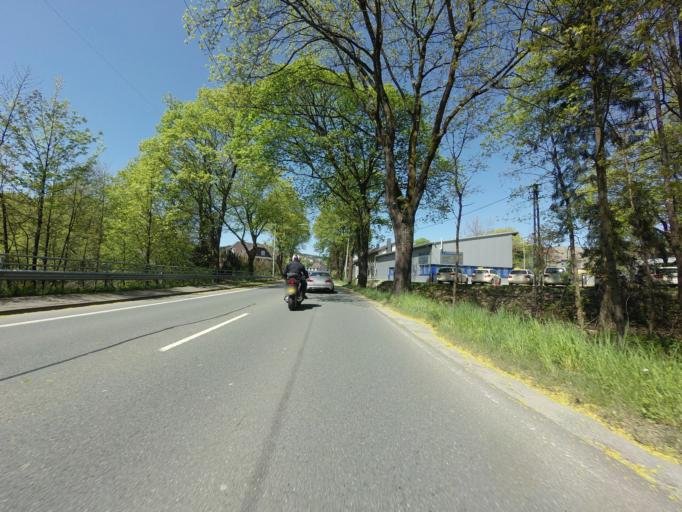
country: DE
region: North Rhine-Westphalia
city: Kreuztal
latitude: 50.9750
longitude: 7.9748
